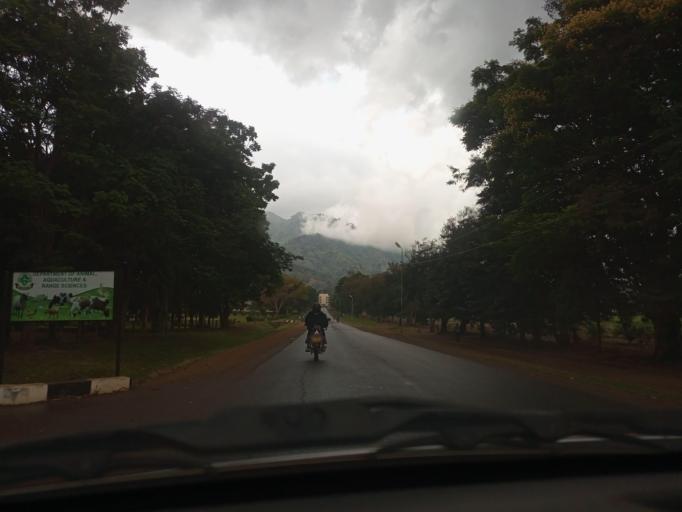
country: TZ
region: Morogoro
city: Morogoro
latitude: -6.8456
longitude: 37.6578
